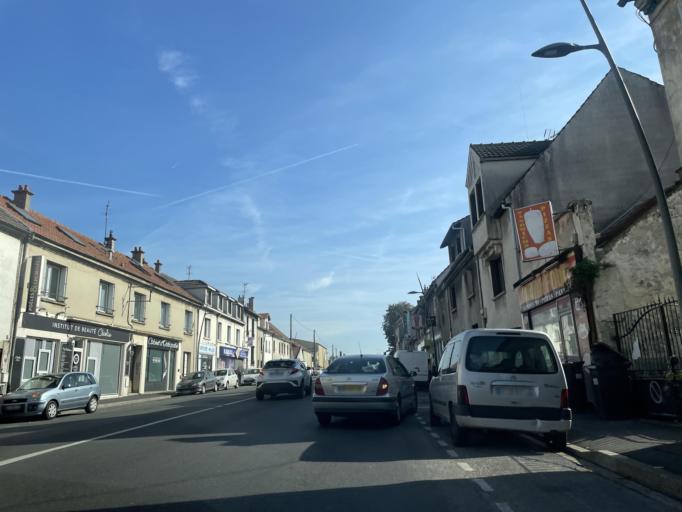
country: FR
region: Ile-de-France
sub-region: Departement de Seine-et-Marne
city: Trilport
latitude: 48.9577
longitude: 2.9475
